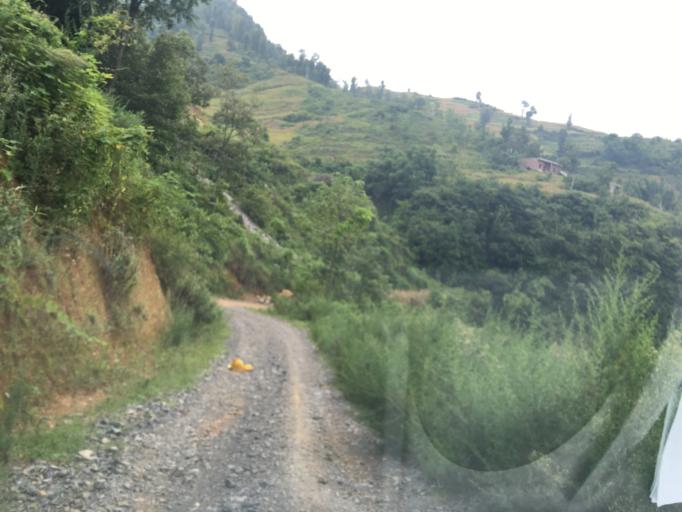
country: CN
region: Guangxi Zhuangzu Zizhiqu
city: Xinzhou
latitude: 25.1713
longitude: 105.7324
